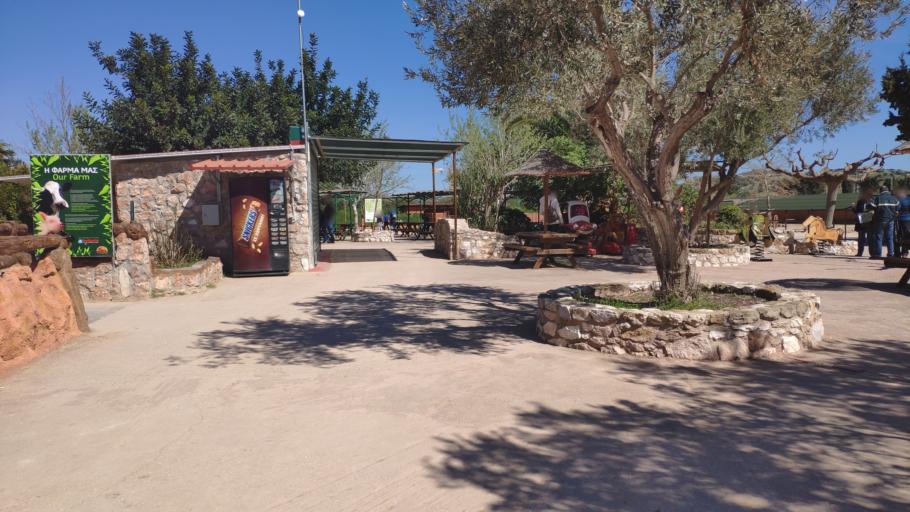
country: GR
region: Attica
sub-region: Nomarchia Anatolikis Attikis
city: Spata
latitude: 37.9808
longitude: 23.9108
